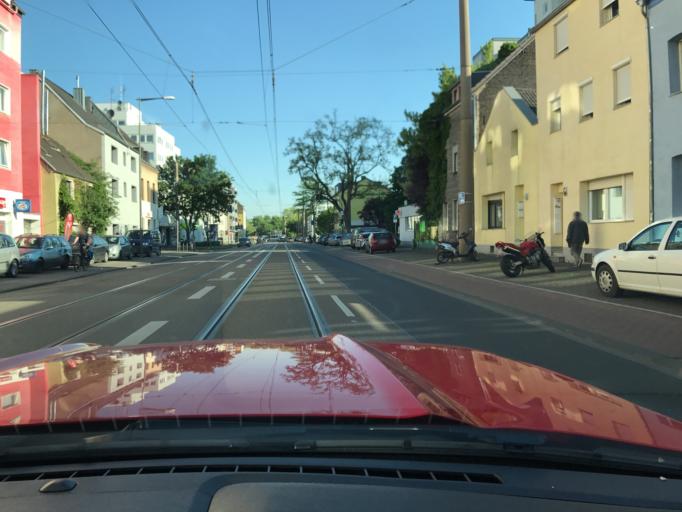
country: DE
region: North Rhine-Westphalia
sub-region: Regierungsbezirk Koln
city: Bilderstoeckchen
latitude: 50.9879
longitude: 6.9448
